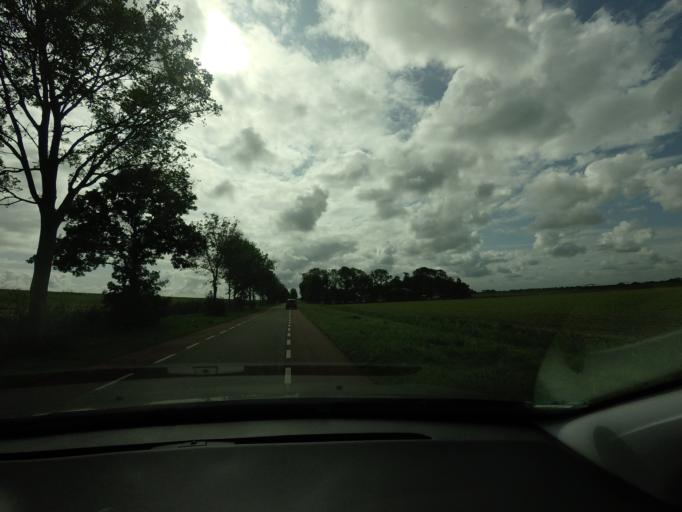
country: NL
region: North Holland
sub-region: Gemeente Medemblik
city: Medemblik
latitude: 52.7967
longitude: 5.1053
